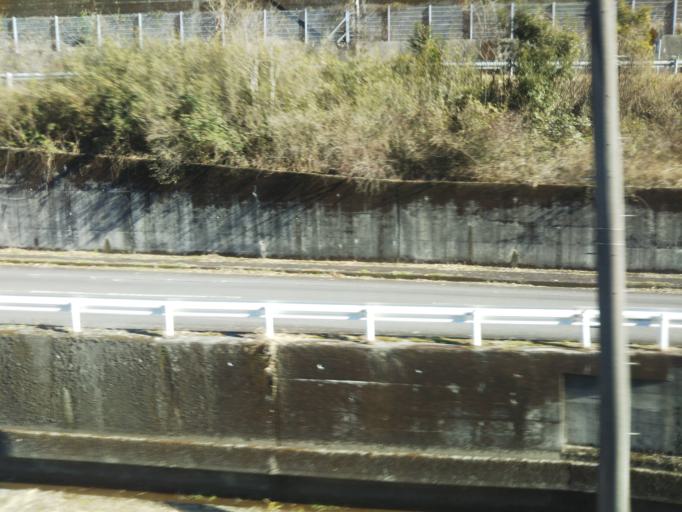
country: JP
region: Kochi
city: Nakamura
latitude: 33.1032
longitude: 133.0986
